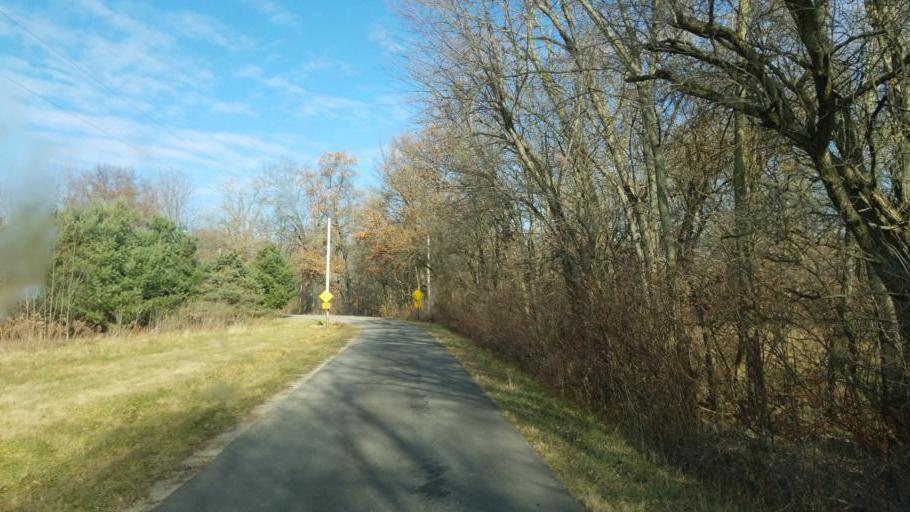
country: US
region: Ohio
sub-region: Marion County
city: Prospect
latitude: 40.5462
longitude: -83.2203
